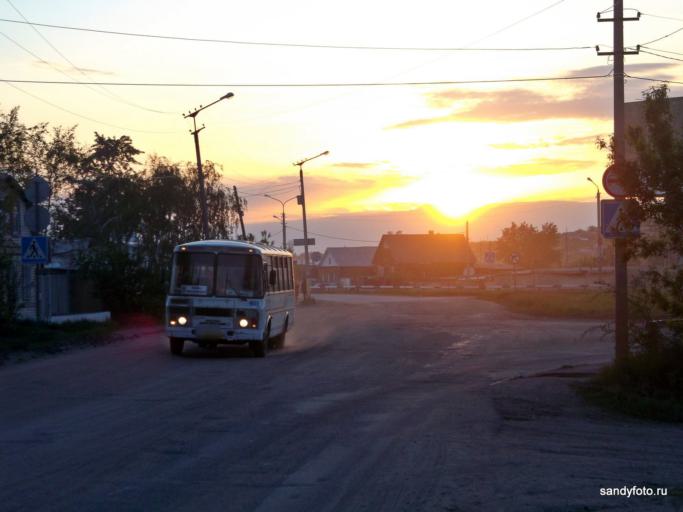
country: RU
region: Chelyabinsk
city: Troitsk
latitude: 54.0892
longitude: 61.5743
